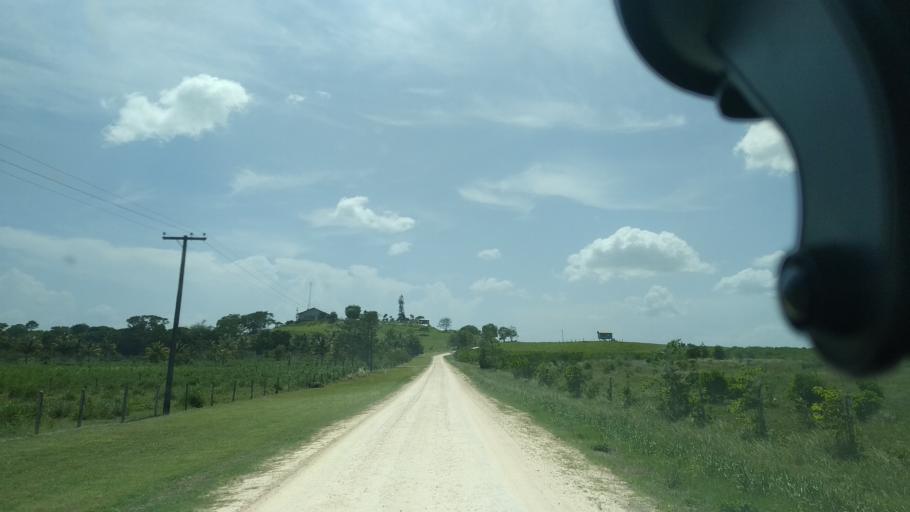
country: BZ
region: Cayo
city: San Ignacio
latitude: 17.3000
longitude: -89.0500
